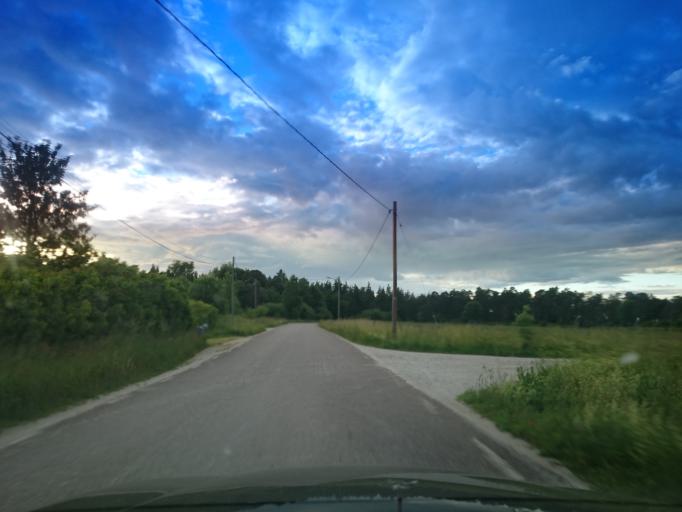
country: SE
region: Gotland
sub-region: Gotland
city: Visby
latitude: 57.5365
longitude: 18.3916
